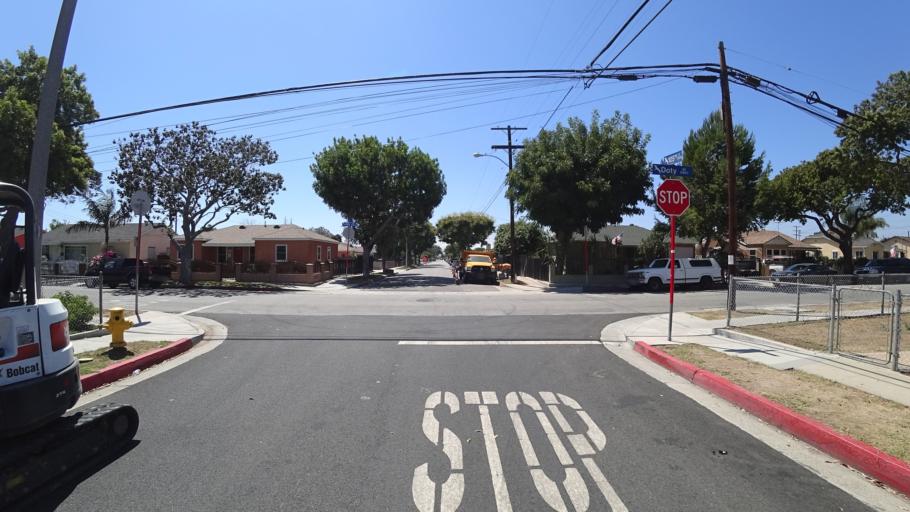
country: US
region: California
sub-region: Los Angeles County
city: Lennox
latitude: 33.9409
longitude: -118.3396
